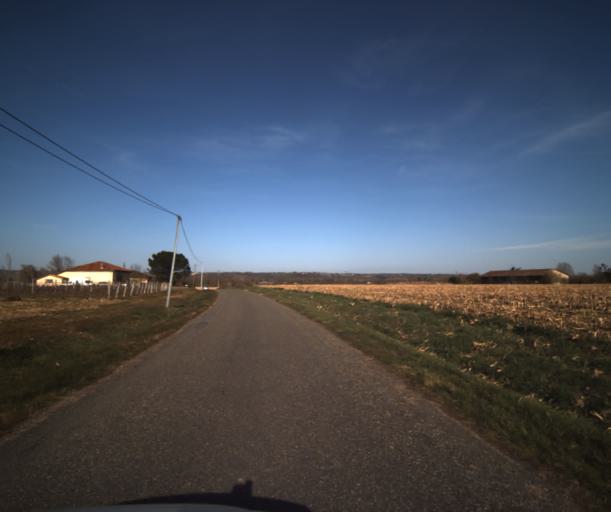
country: FR
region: Midi-Pyrenees
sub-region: Departement du Tarn-et-Garonne
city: Labastide-Saint-Pierre
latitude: 43.9228
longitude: 1.3513
